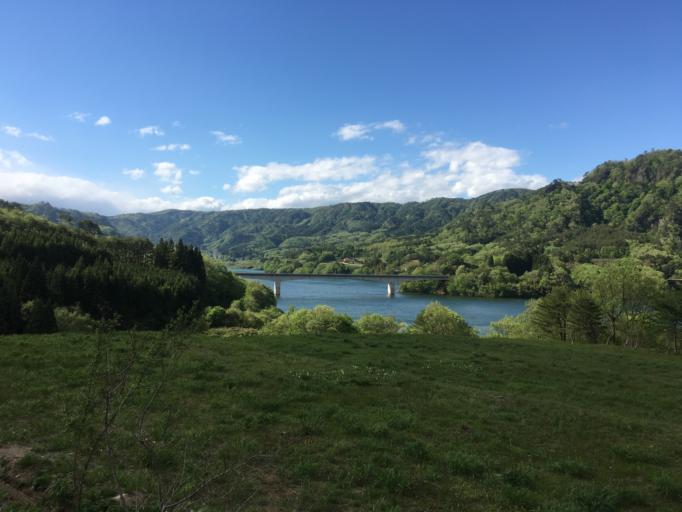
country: JP
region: Miyagi
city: Marumori
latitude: 37.7204
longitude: 140.8215
